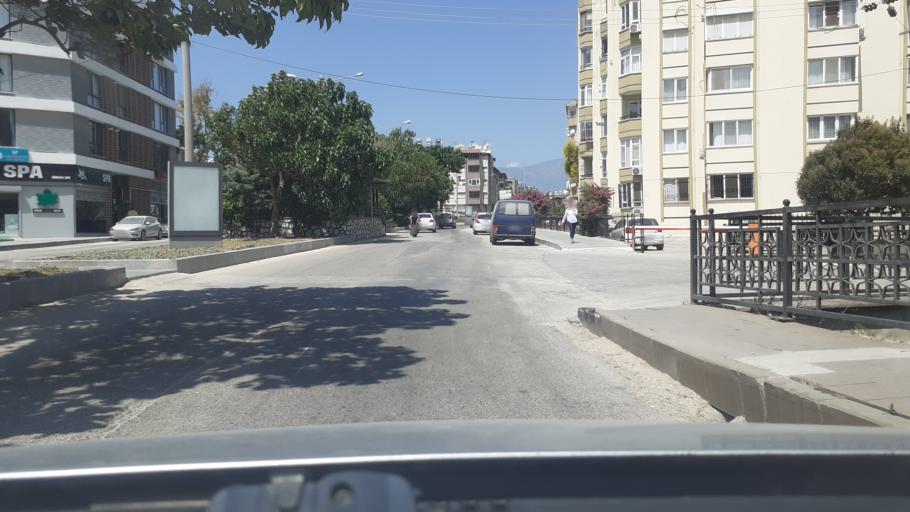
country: TR
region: Hatay
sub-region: Antakya Ilcesi
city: Antakya
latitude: 36.1956
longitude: 36.1563
